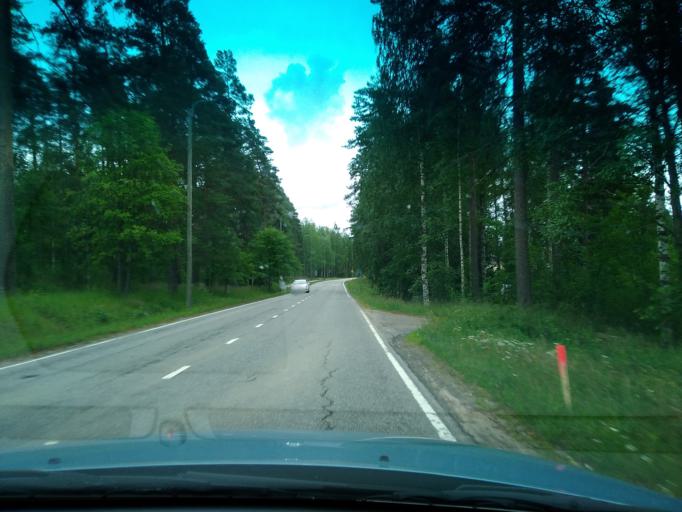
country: FI
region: Central Finland
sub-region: Keuruu
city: Multia
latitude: 62.4131
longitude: 24.7938
